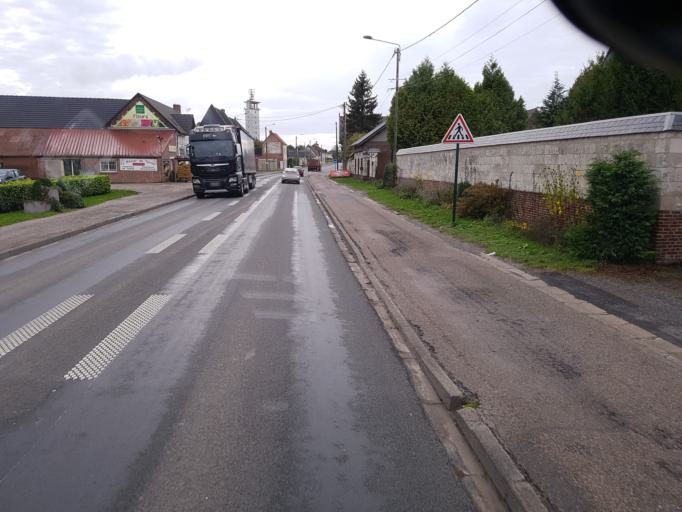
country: FR
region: Nord-Pas-de-Calais
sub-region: Departement du Pas-de-Calais
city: Avesnes-le-Comte
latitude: 50.2135
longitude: 2.5596
